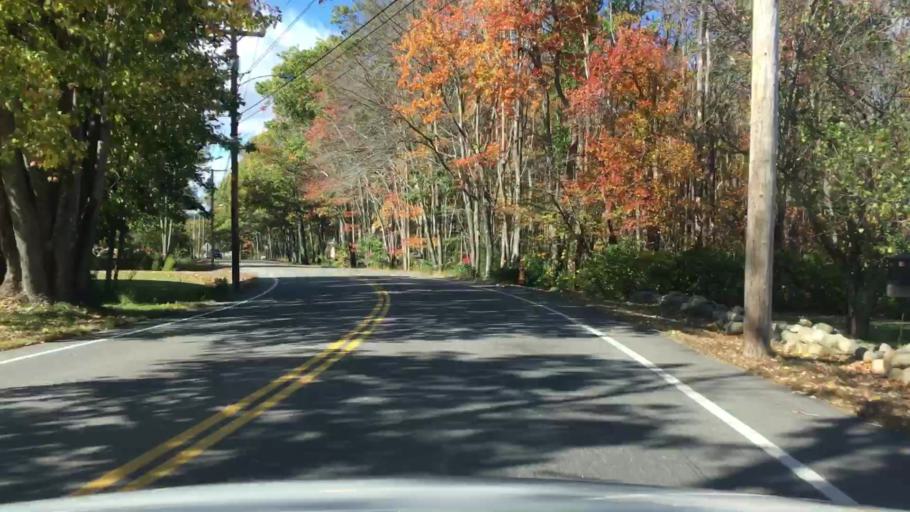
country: US
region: Maine
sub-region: York County
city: Biddeford
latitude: 43.4711
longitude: -70.4526
